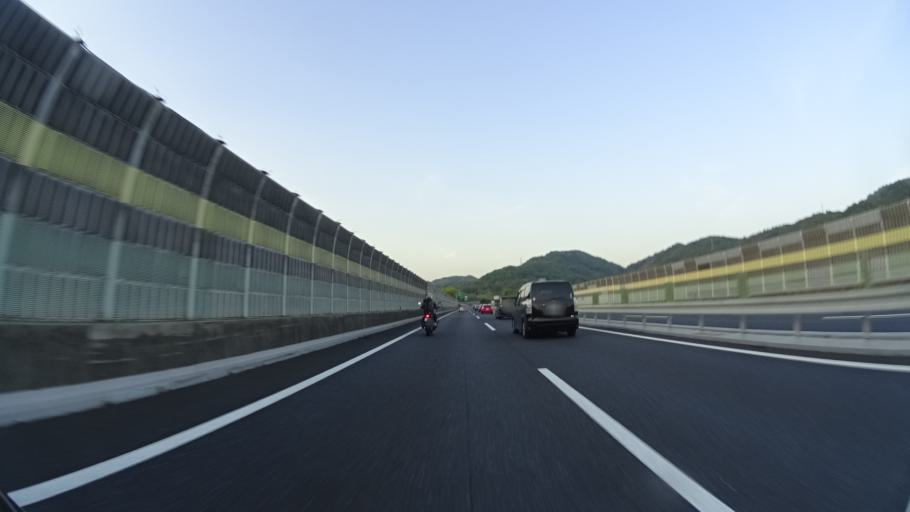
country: JP
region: Okayama
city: Okayama-shi
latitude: 34.7480
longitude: 134.0309
